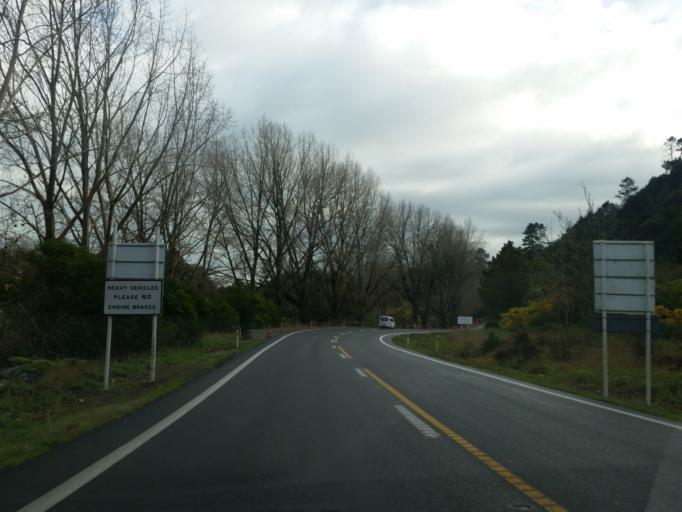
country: NZ
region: Waikato
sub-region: Hauraki District
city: Paeroa
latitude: -37.4168
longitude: 175.7174
